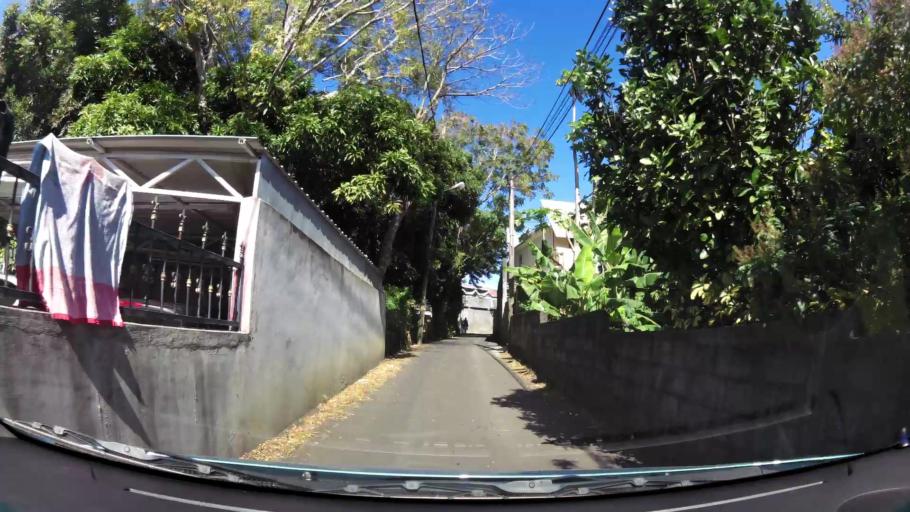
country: MU
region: Plaines Wilhems
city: Vacoas
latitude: -20.3185
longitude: 57.4866
